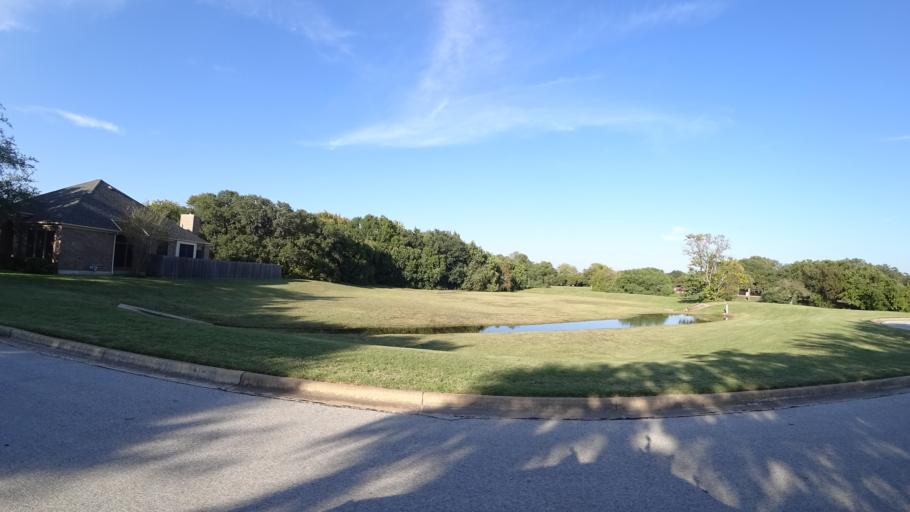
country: US
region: Texas
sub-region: Travis County
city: Shady Hollow
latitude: 30.2182
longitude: -97.8518
